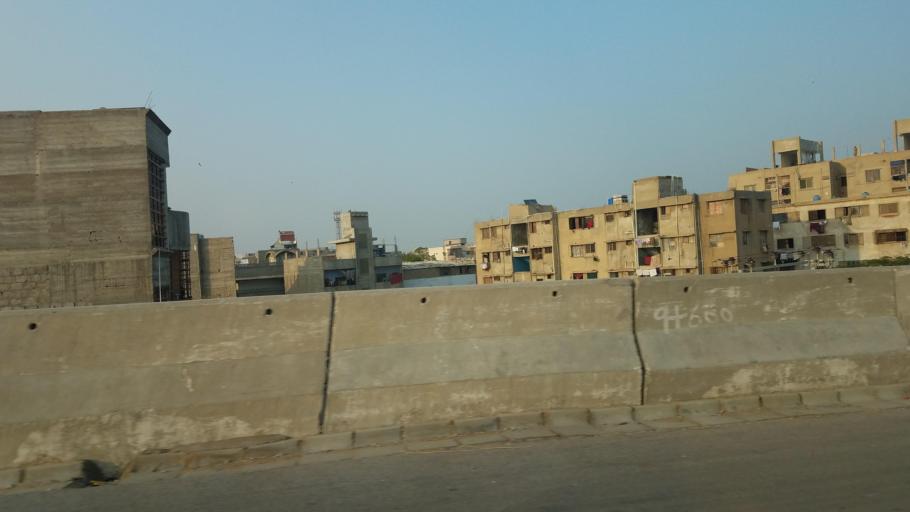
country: PK
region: Sindh
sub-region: Karachi District
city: Karachi
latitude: 24.8914
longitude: 67.0322
